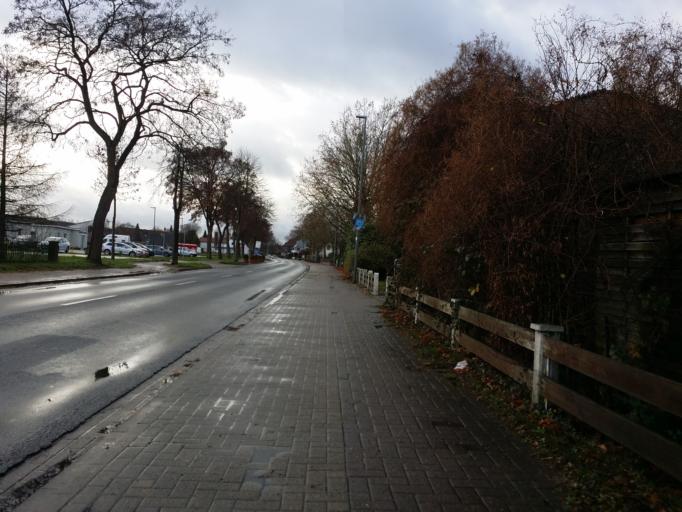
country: DE
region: Lower Saxony
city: Stuhr
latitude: 52.9891
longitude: 8.8010
